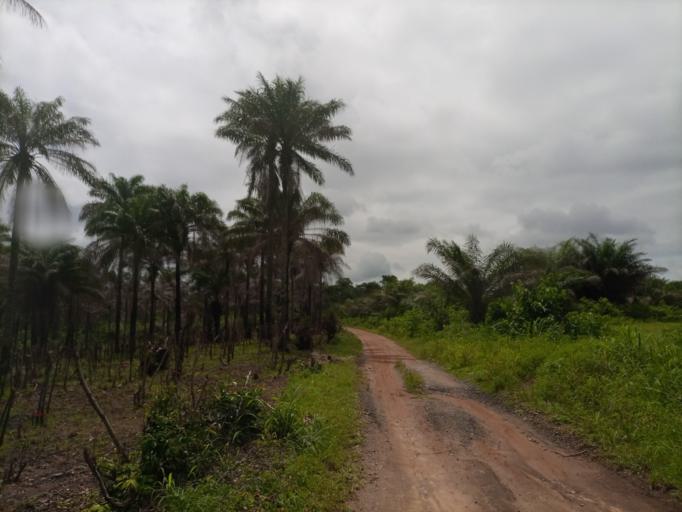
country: SL
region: Northern Province
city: Sawkta
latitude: 8.6547
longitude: -13.1782
